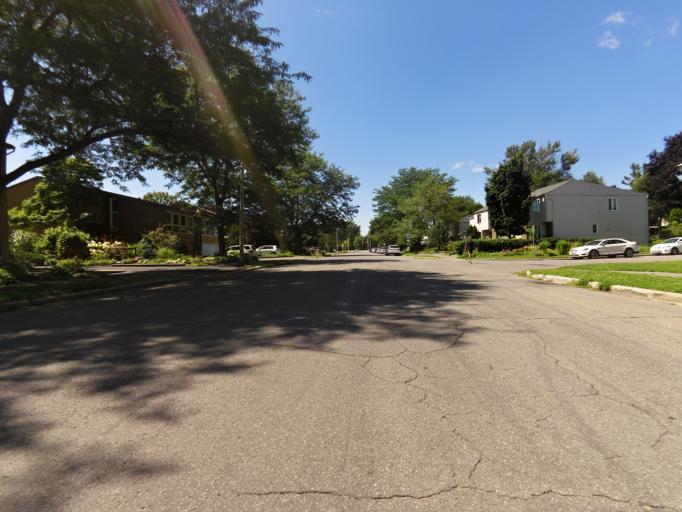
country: CA
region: Ontario
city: Ottawa
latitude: 45.3650
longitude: -75.6859
